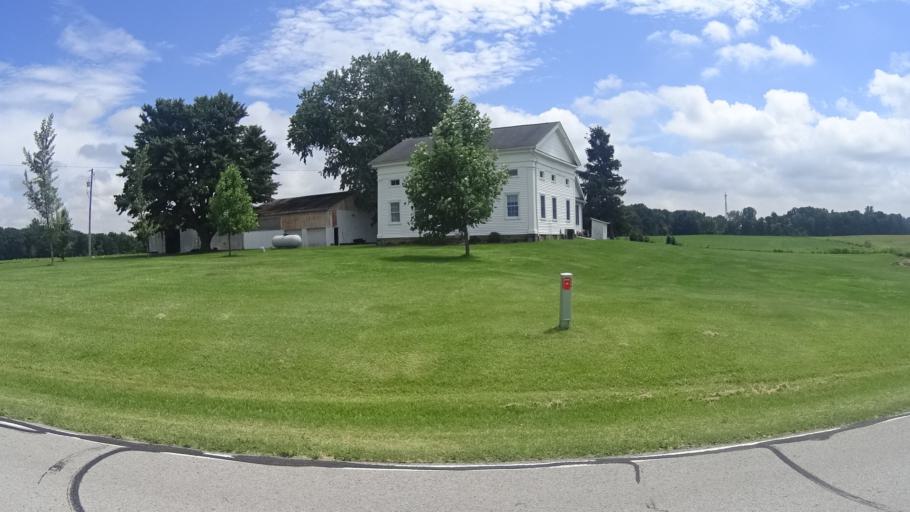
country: US
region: Ohio
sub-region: Erie County
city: Milan
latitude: 41.3146
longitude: -82.5692
